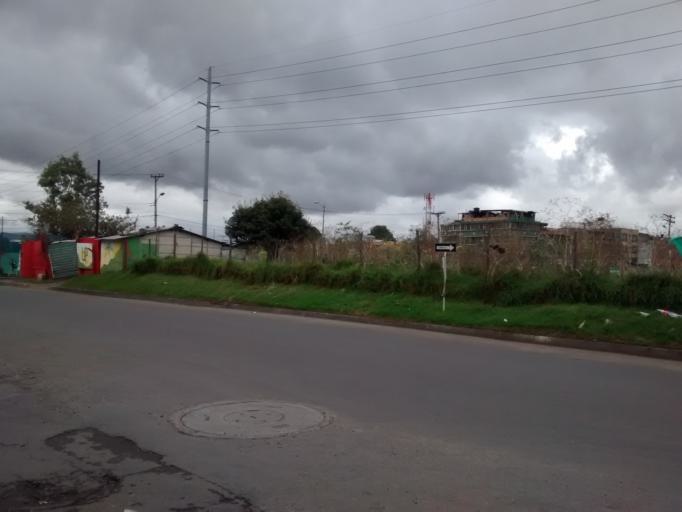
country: CO
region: Bogota D.C.
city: Barrio San Luis
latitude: 4.7044
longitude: -74.1124
